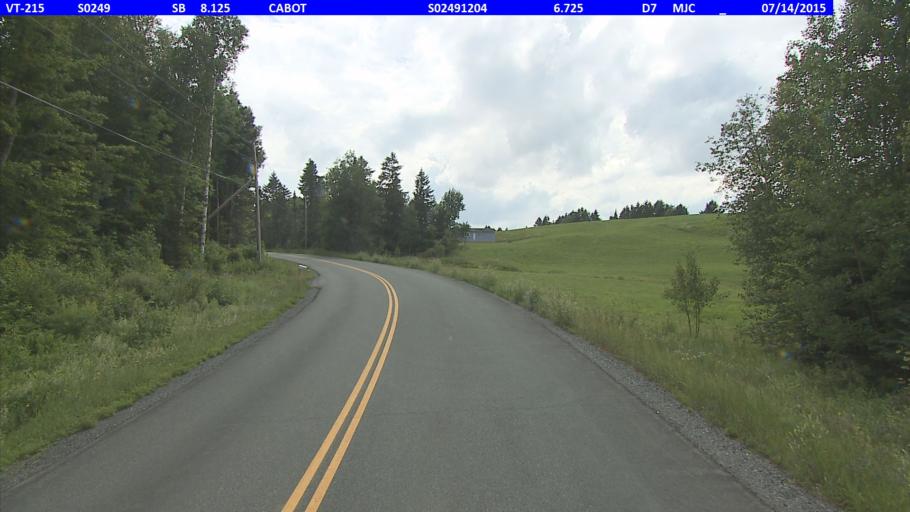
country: US
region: Vermont
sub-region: Caledonia County
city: Hardwick
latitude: 44.4420
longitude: -72.2702
